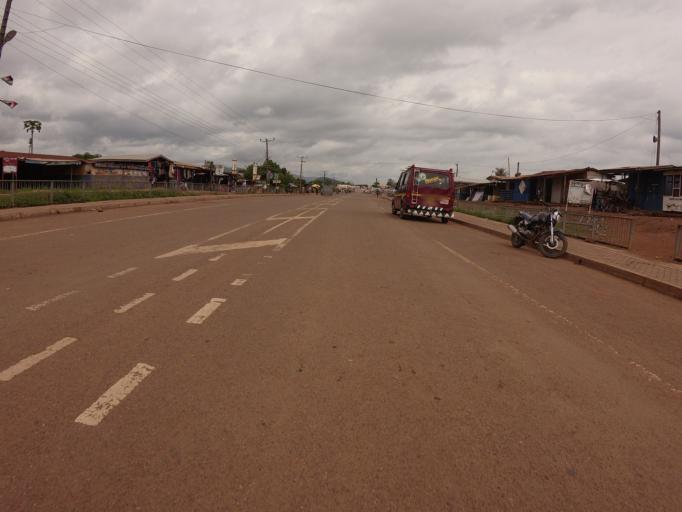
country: TG
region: Centrale
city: Sotouboua
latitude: 8.2678
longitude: 0.5193
